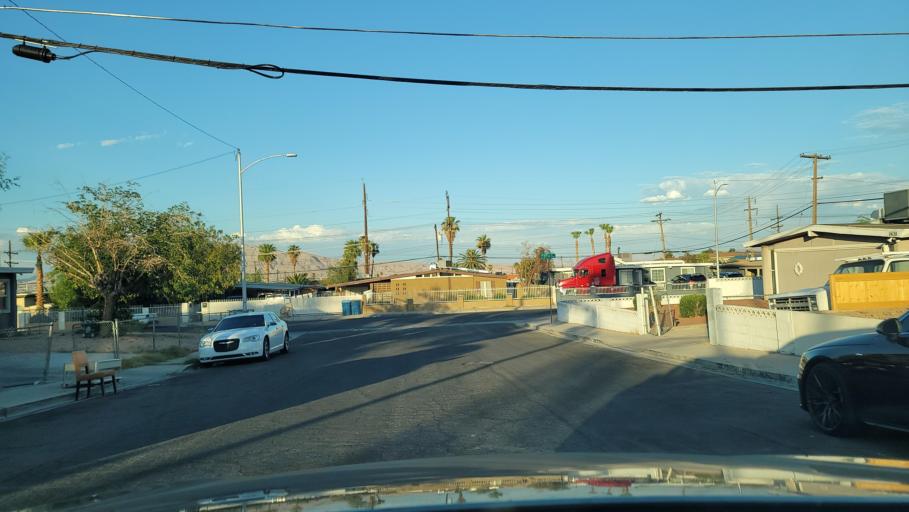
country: US
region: Nevada
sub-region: Clark County
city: Winchester
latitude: 36.1473
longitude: -115.1291
